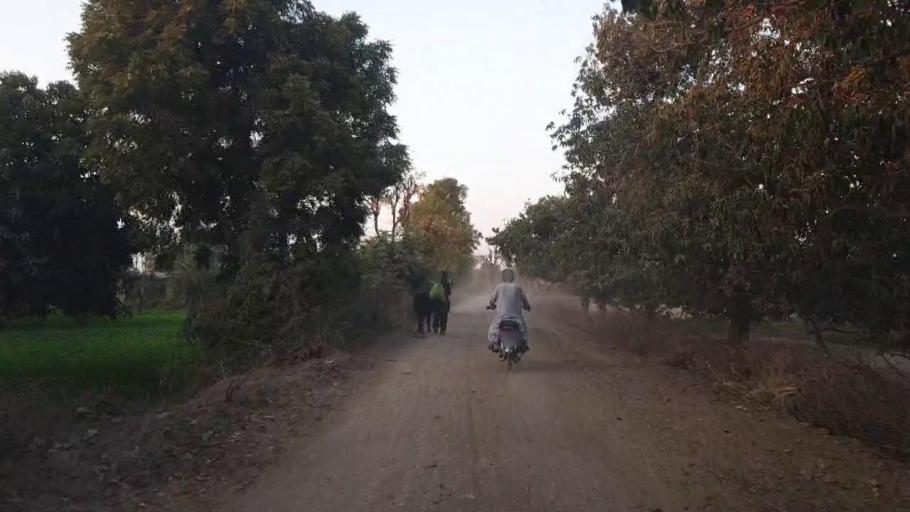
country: PK
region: Sindh
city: Chambar
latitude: 25.4156
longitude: 68.8614
